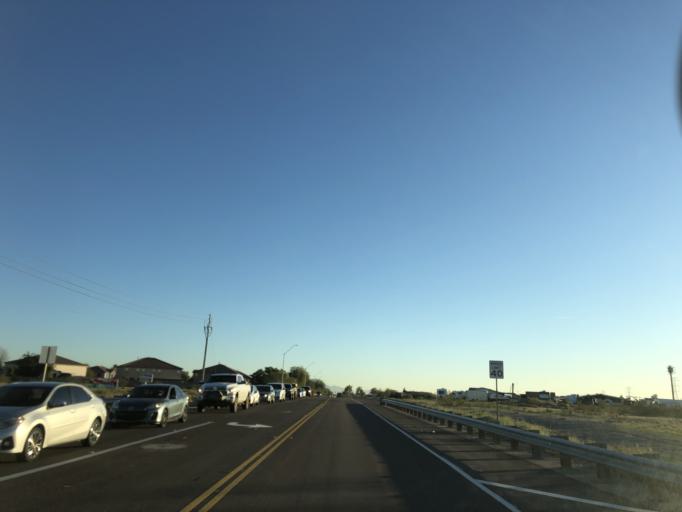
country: US
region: Arizona
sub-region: Maricopa County
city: Sun City West
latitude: 33.6959
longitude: -112.2897
